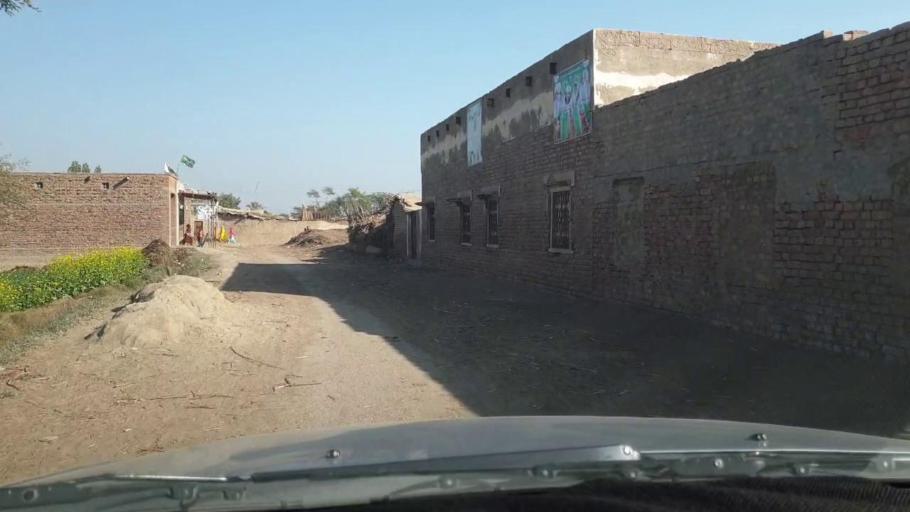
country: PK
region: Sindh
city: Mirpur Mathelo
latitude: 27.9723
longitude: 69.5559
